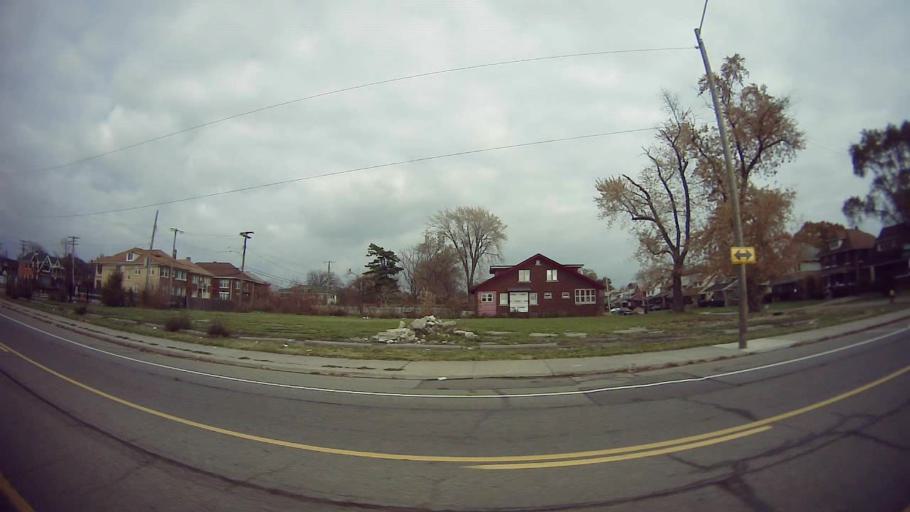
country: US
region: Michigan
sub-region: Wayne County
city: Highland Park
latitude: 42.3666
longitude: -83.1043
